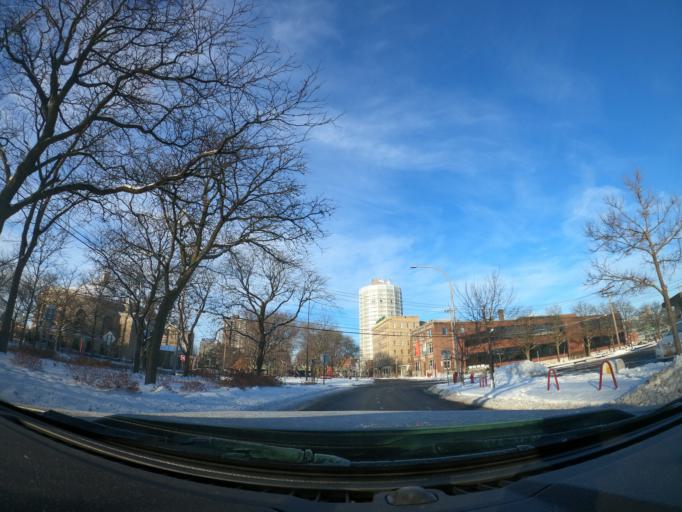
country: US
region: New York
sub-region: Onondaga County
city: Syracuse
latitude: 43.0472
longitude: -76.1396
